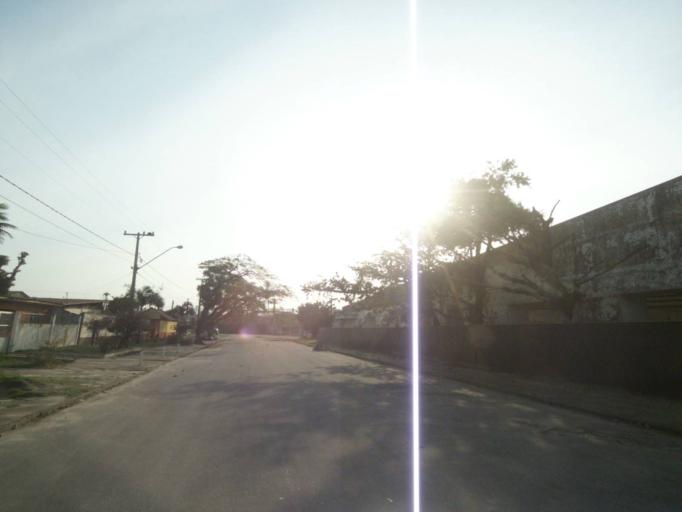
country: BR
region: Parana
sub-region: Paranagua
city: Paranagua
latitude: -25.5066
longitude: -48.5322
